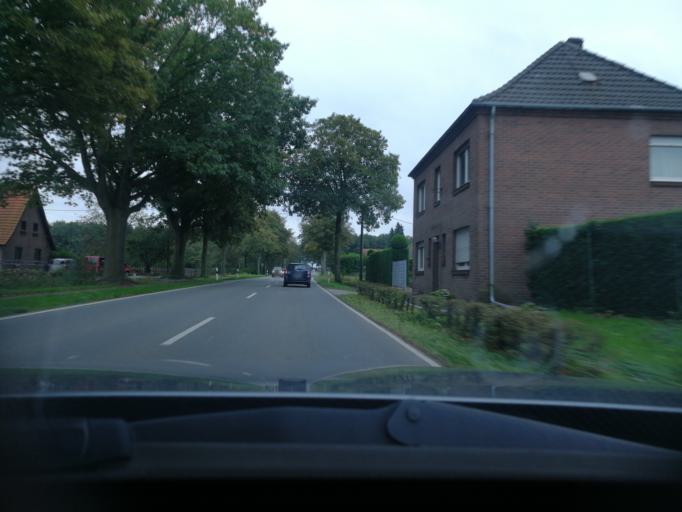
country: DE
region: North Rhine-Westphalia
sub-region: Regierungsbezirk Dusseldorf
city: Kevelaer
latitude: 51.5197
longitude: 6.2431
